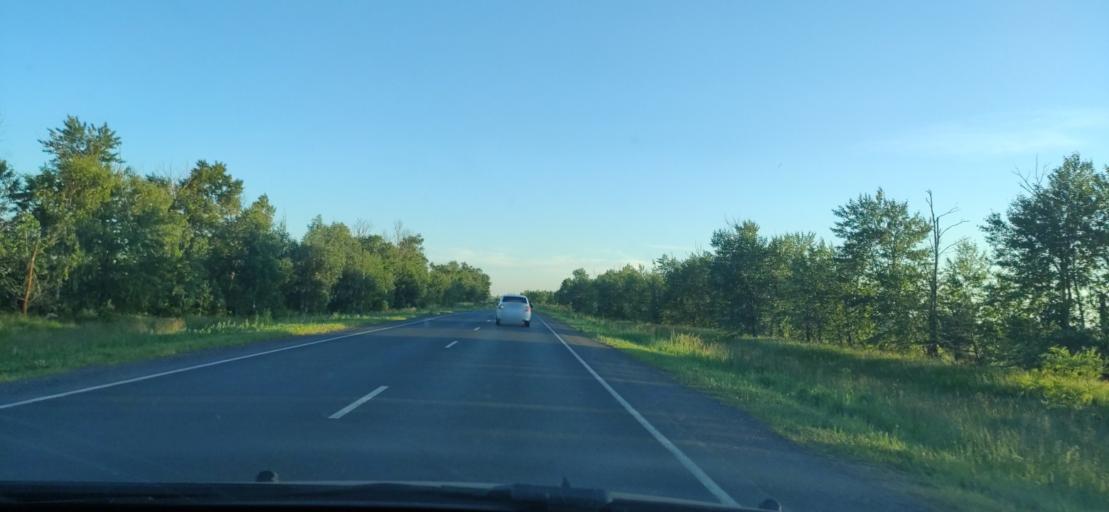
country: RU
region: Ulyanovsk
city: Cherdakly
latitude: 54.4013
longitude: 48.8625
